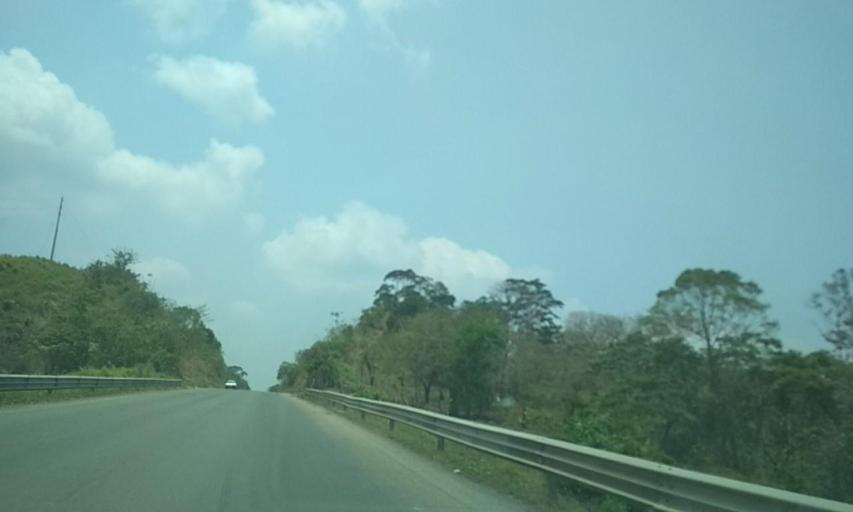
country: MX
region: Tabasco
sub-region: Huimanguillo
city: Francisco Rueda
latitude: 17.6767
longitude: -93.8798
